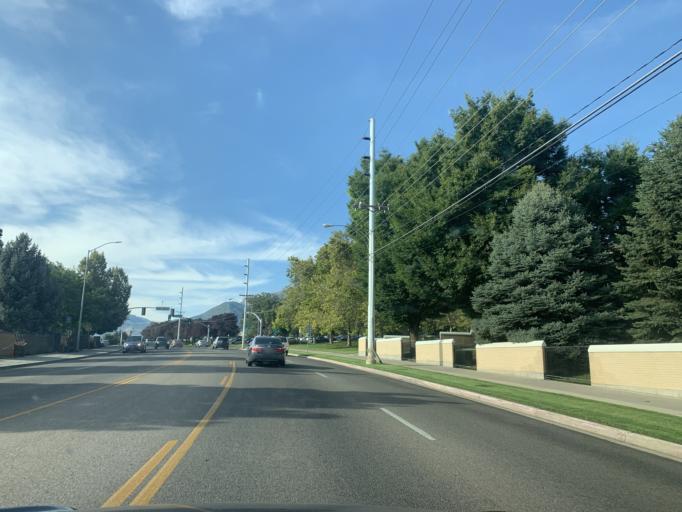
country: US
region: Utah
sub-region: Utah County
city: Provo
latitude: 40.2591
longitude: -111.6431
